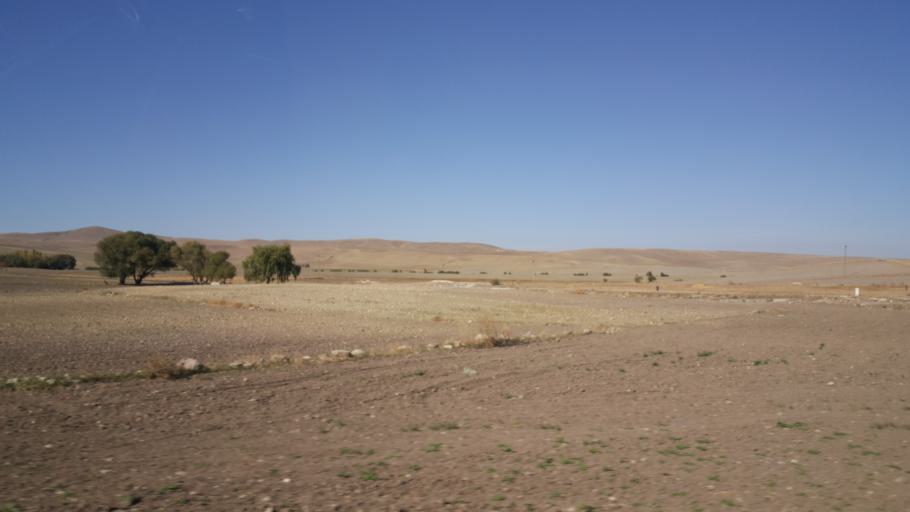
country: TR
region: Ankara
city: Yenice
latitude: 39.3729
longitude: 32.7249
